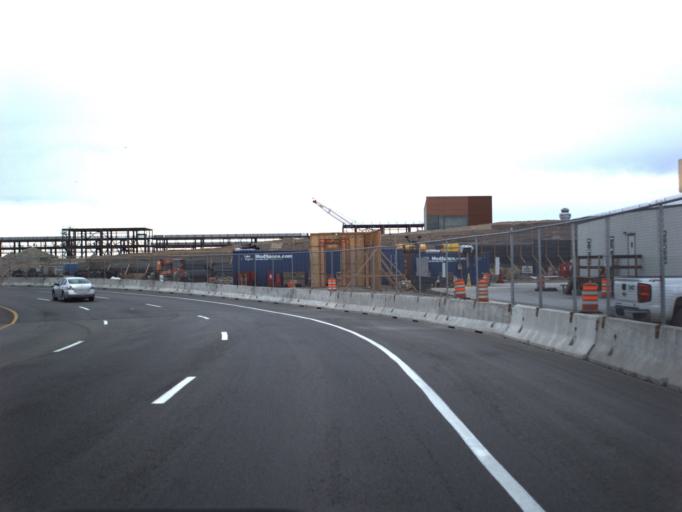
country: US
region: Utah
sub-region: Salt Lake County
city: West Valley City
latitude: 40.7823
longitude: -111.9887
